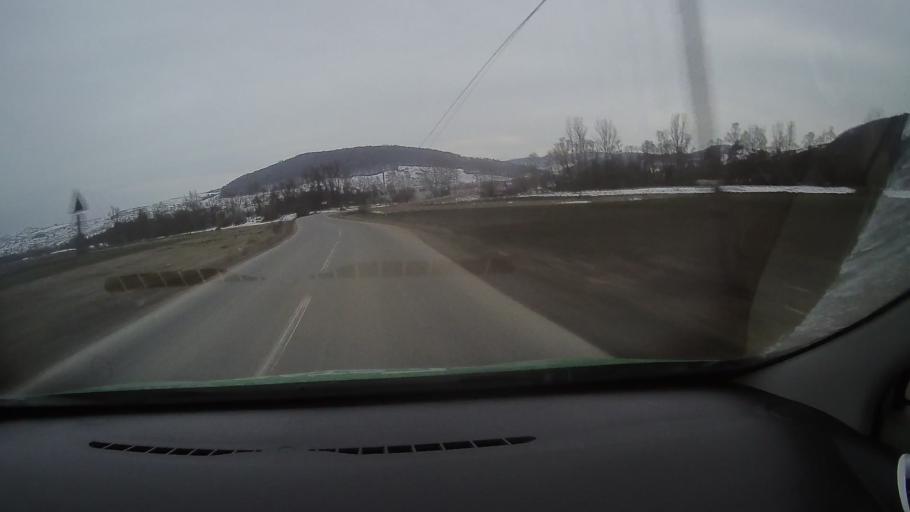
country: RO
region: Harghita
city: Taureni
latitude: 46.2639
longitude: 25.2512
